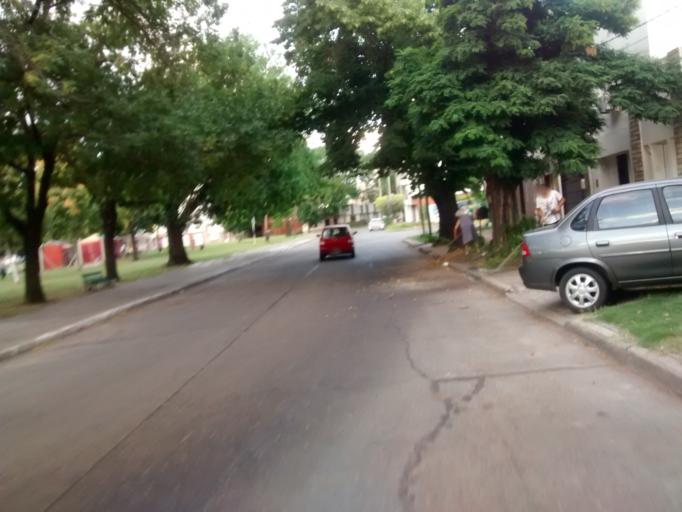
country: AR
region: Buenos Aires
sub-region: Partido de La Plata
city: La Plata
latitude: -34.9380
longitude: -57.9469
